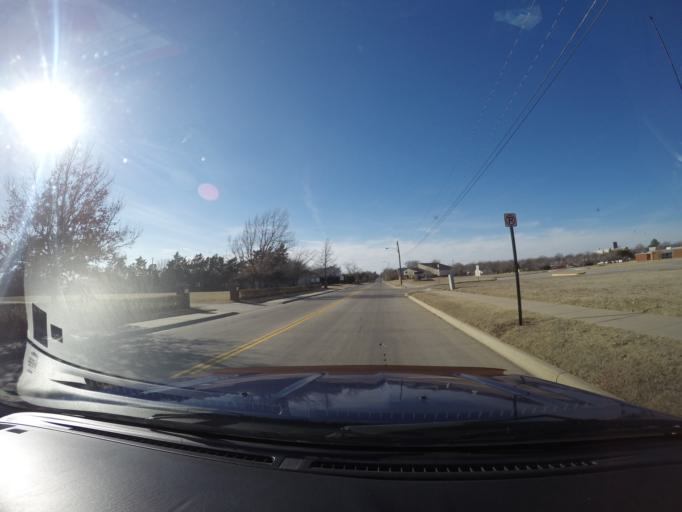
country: US
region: Kansas
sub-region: Harvey County
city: Newton
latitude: 38.0428
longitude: -97.3291
